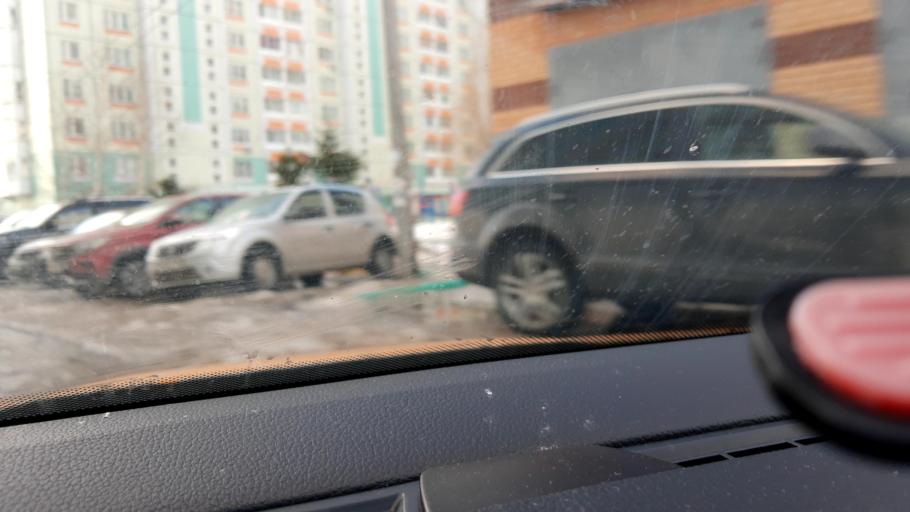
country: RU
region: Moskovskaya
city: Dubrovitsy
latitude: 55.4182
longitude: 37.4773
